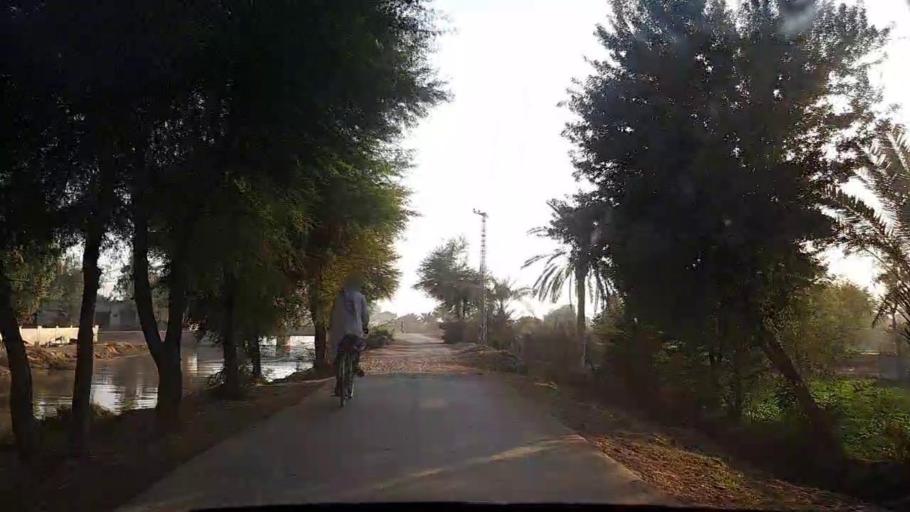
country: PK
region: Sindh
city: Sobhadero
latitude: 27.3887
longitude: 68.3832
